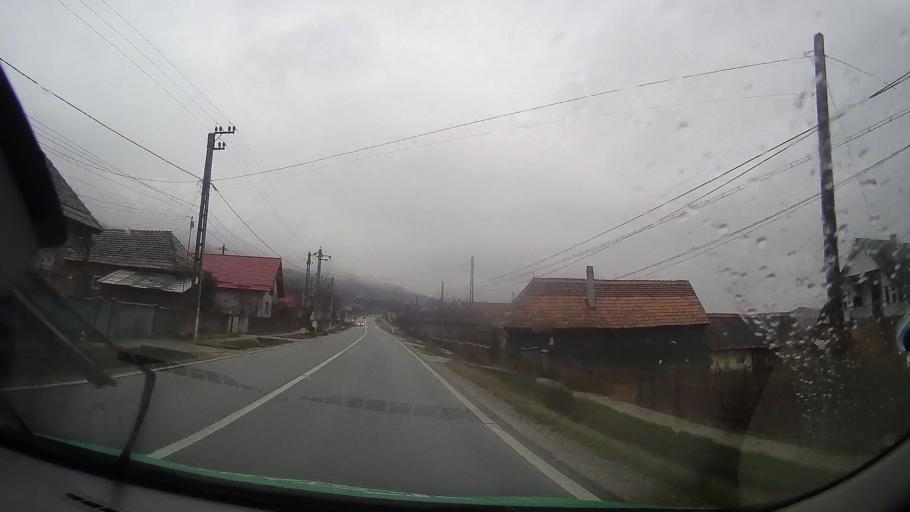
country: RO
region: Bistrita-Nasaud
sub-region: Comuna Galatii Bistritei
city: Galatii Bistritei
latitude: 46.9952
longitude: 24.4164
